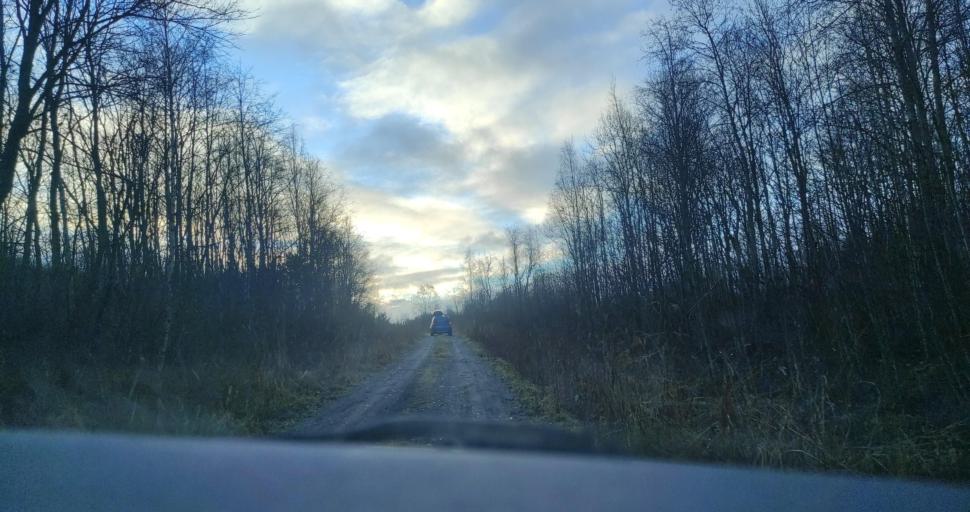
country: RU
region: Republic of Karelia
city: Pitkyaranta
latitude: 61.7299
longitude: 31.3800
